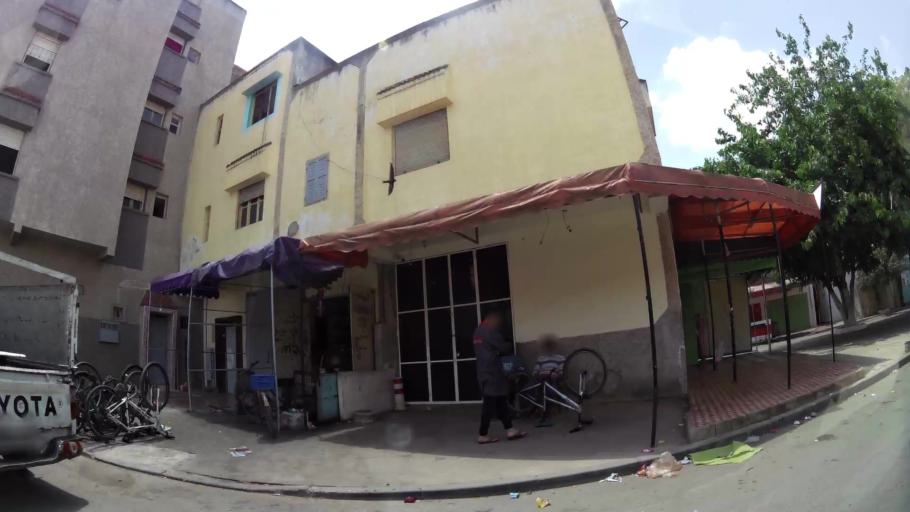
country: MA
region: Rabat-Sale-Zemmour-Zaer
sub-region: Khemisset
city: Tiflet
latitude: 34.0031
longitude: -6.5313
